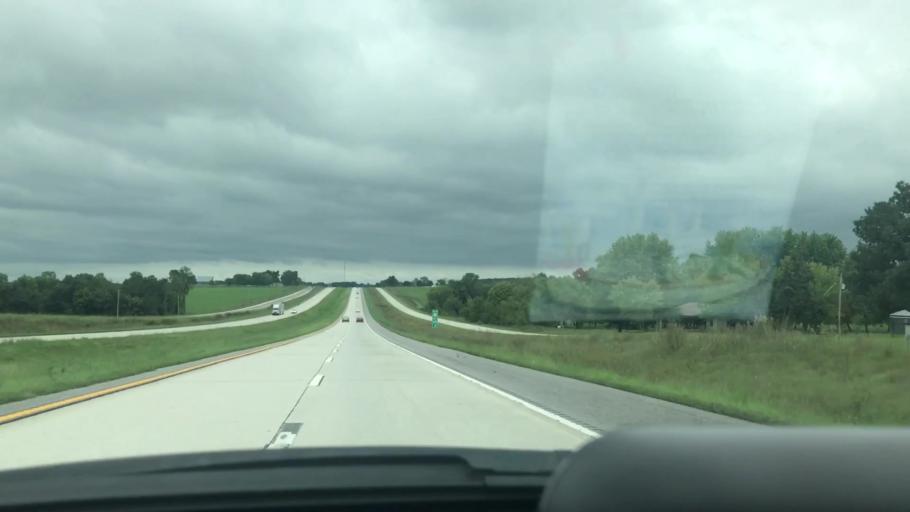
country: US
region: Missouri
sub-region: Greene County
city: Fair Grove
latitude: 37.4278
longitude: -93.1449
